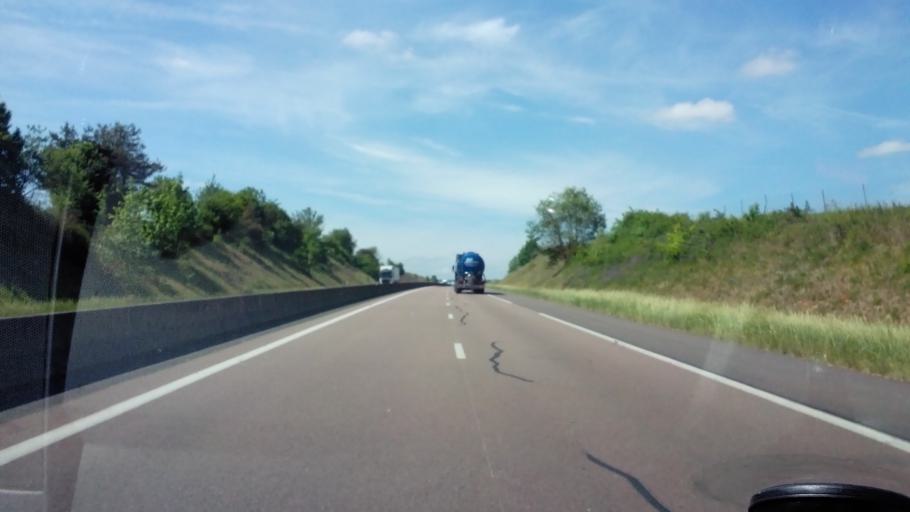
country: FR
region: Lorraine
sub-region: Departement de Meurthe-et-Moselle
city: Colombey-les-Belles
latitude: 48.4789
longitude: 5.8917
